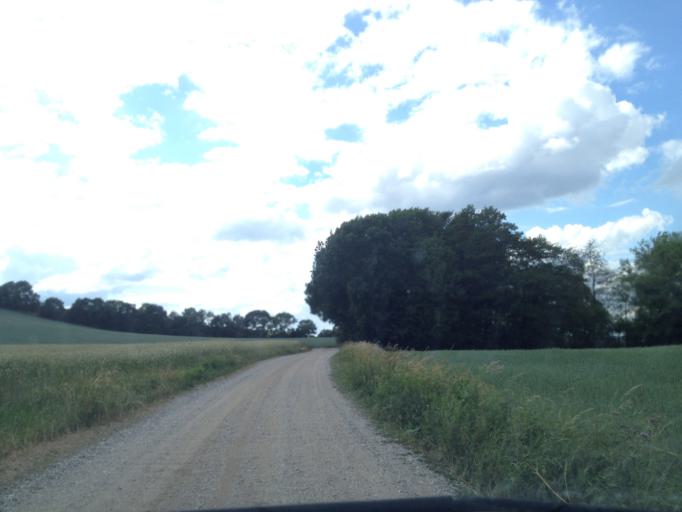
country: DK
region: Central Jutland
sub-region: Syddjurs Kommune
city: Ronde
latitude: 56.1991
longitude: 10.4857
